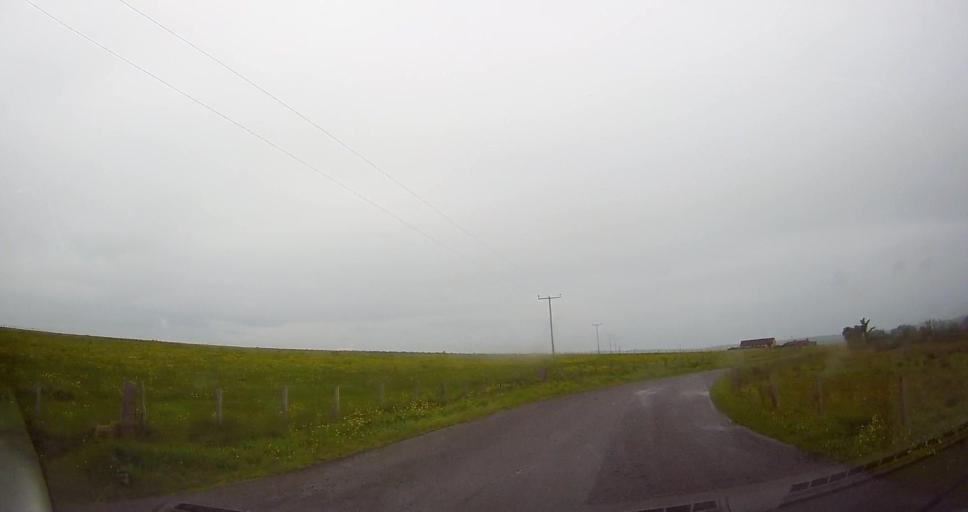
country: GB
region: Scotland
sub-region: Orkney Islands
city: Stromness
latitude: 59.0752
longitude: -3.2050
